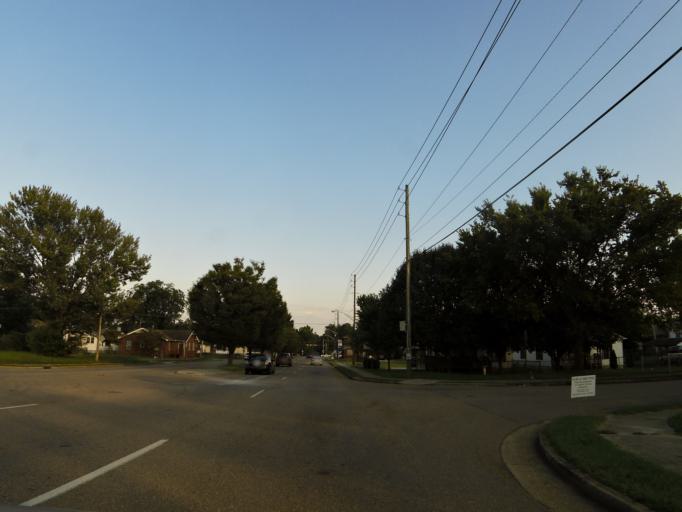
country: US
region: Tennessee
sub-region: Knox County
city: Knoxville
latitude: 35.9886
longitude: -83.8960
